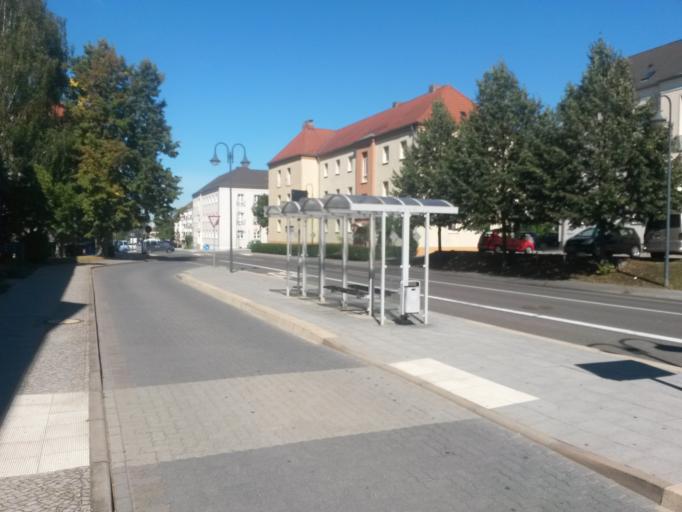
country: DE
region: Brandenburg
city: Prenzlau
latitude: 53.3145
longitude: 13.8575
